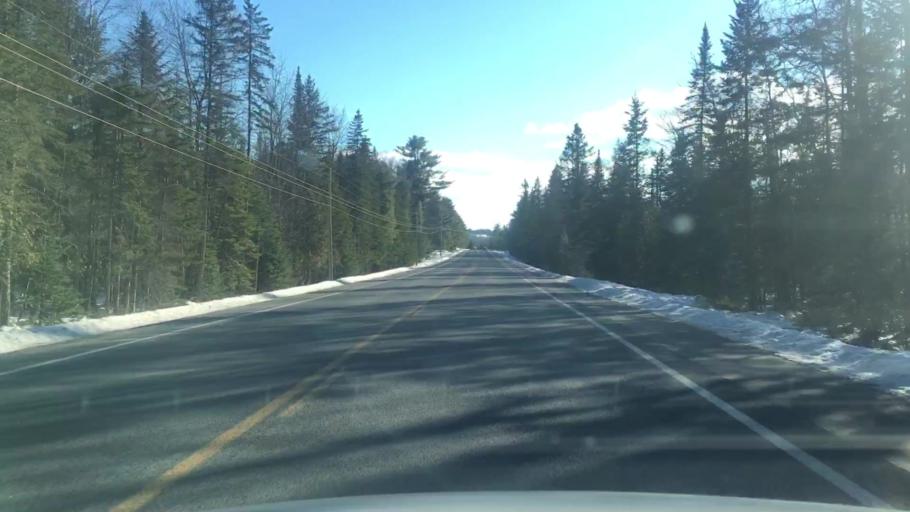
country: US
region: Maine
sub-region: Somerset County
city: Madison
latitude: 44.9187
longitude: -69.8247
